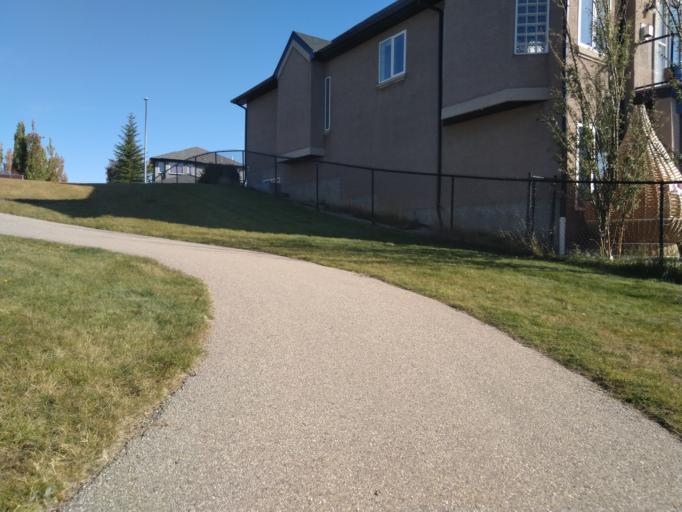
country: CA
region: Alberta
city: Calgary
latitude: 51.1533
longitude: -114.0930
